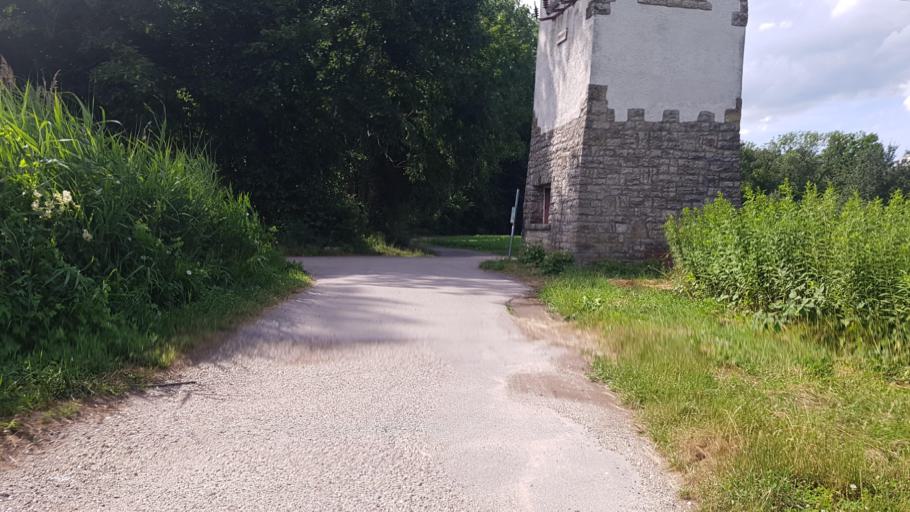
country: DE
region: Baden-Wuerttemberg
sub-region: Karlsruhe Region
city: Weingarten
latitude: 49.0329
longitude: 8.5148
